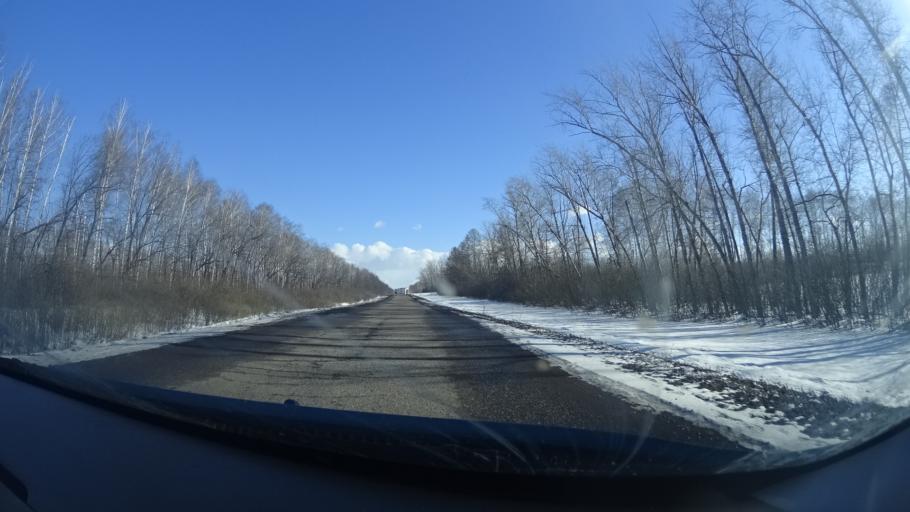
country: RU
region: Bashkortostan
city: Chishmy
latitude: 54.5975
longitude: 55.3538
